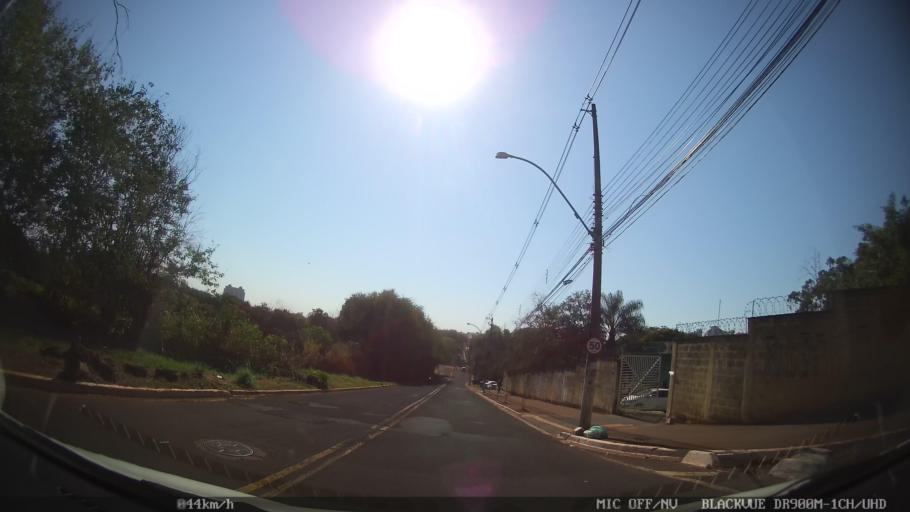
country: BR
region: Sao Paulo
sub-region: Ribeirao Preto
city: Ribeirao Preto
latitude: -21.2104
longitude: -47.8254
